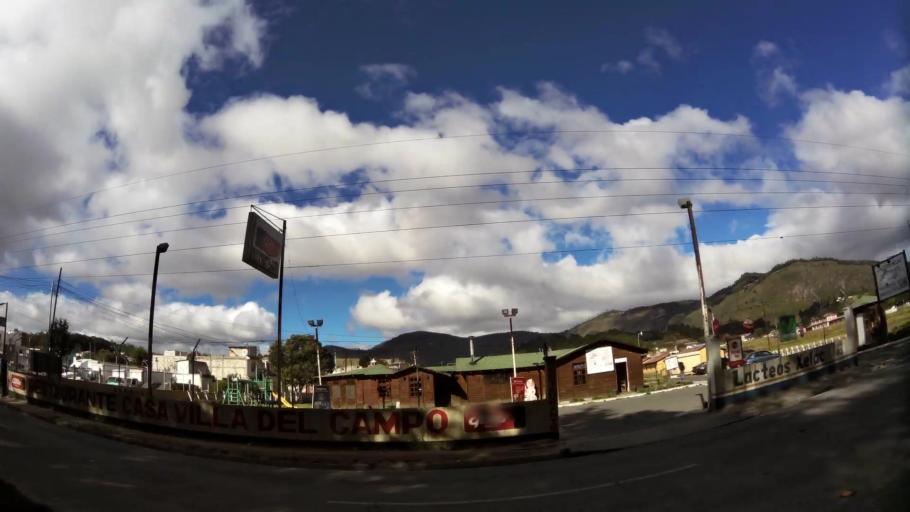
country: GT
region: Quetzaltenango
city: Salcaja
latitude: 14.8979
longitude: -91.4535
